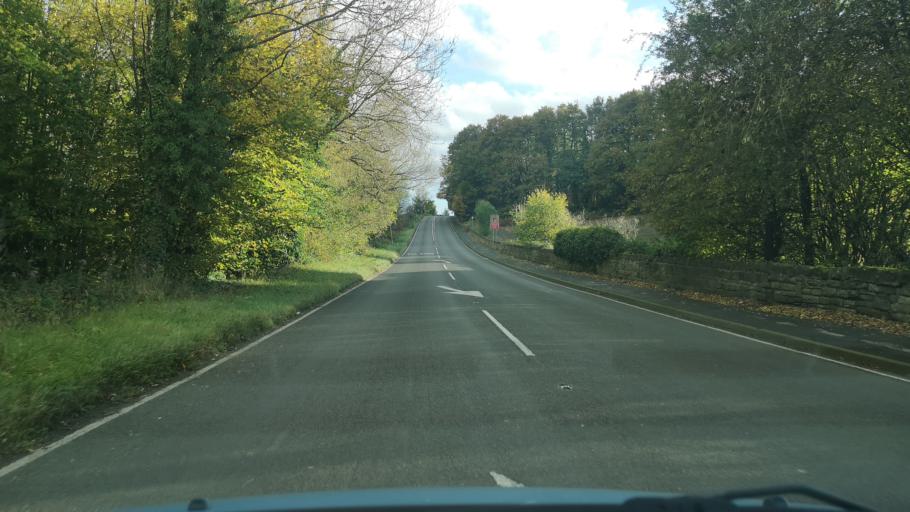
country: GB
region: England
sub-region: City and Borough of Wakefield
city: Woolley
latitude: 53.6188
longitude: -1.4963
